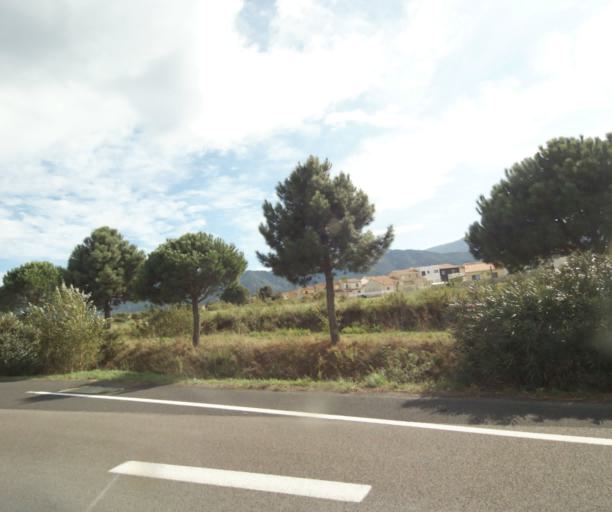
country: FR
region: Languedoc-Roussillon
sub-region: Departement des Pyrenees-Orientales
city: Sant Andreu de Sureda
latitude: 42.5574
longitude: 2.9775
